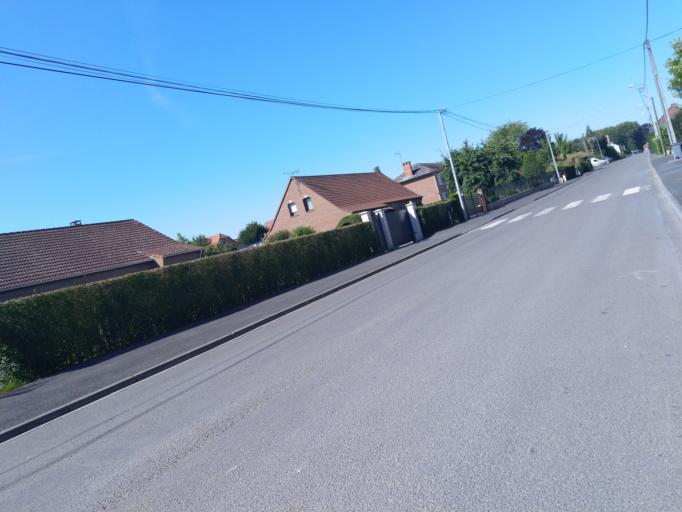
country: FR
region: Nord-Pas-de-Calais
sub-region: Departement du Nord
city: Bavay
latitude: 50.3000
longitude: 3.8059
